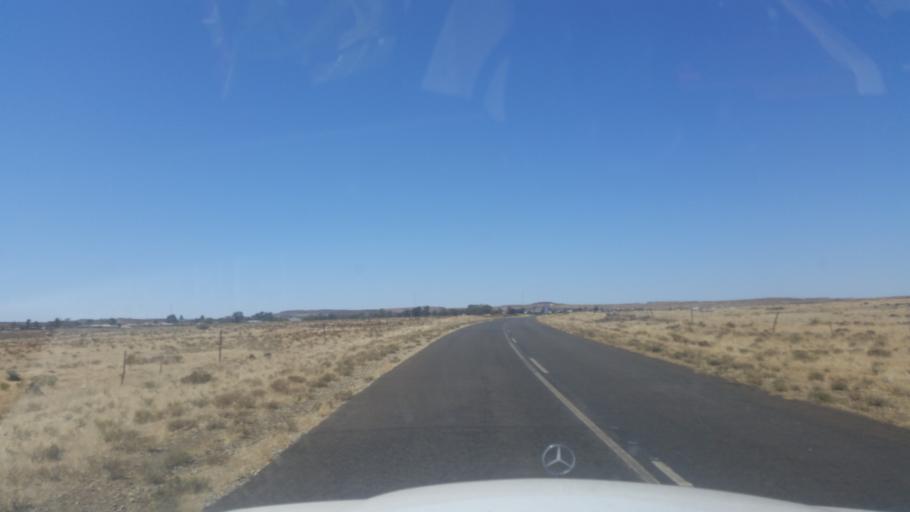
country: ZA
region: Eastern Cape
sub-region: Joe Gqabi District Municipality
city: Burgersdorp
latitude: -30.7637
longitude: 25.7859
